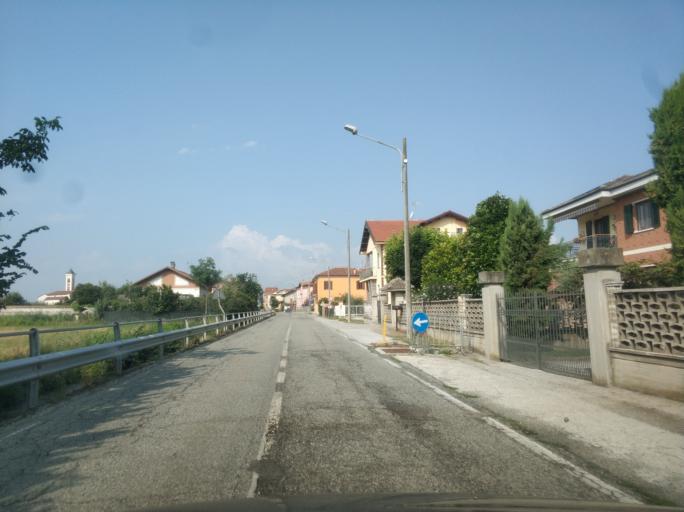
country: IT
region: Piedmont
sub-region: Provincia di Cuneo
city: Montanera
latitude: 44.5124
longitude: 7.6484
